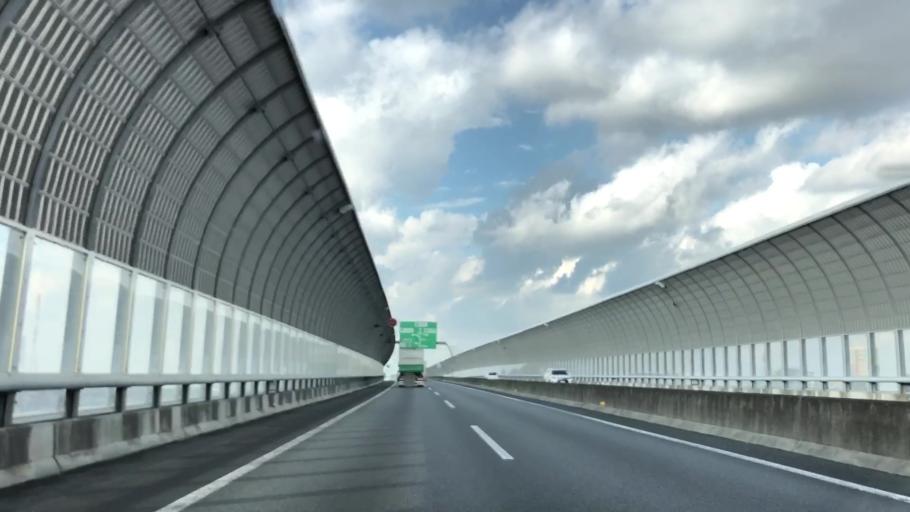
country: JP
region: Saitama
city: Yashio-shi
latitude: 35.8160
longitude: 139.8747
